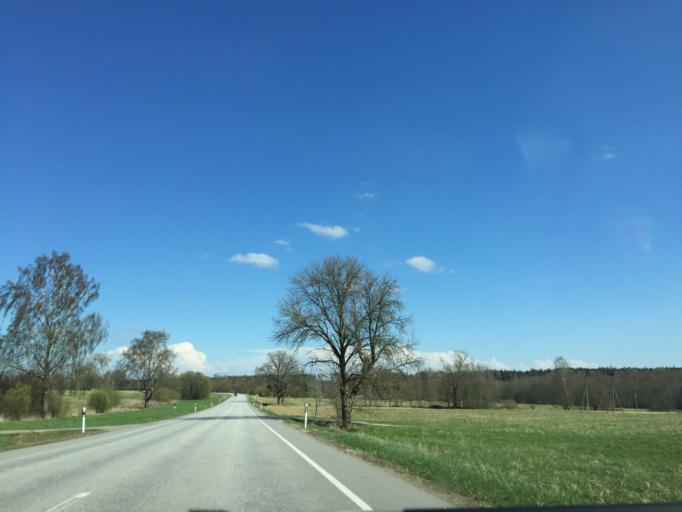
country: EE
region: Valgamaa
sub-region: Valga linn
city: Valga
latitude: 57.8530
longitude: 26.1531
